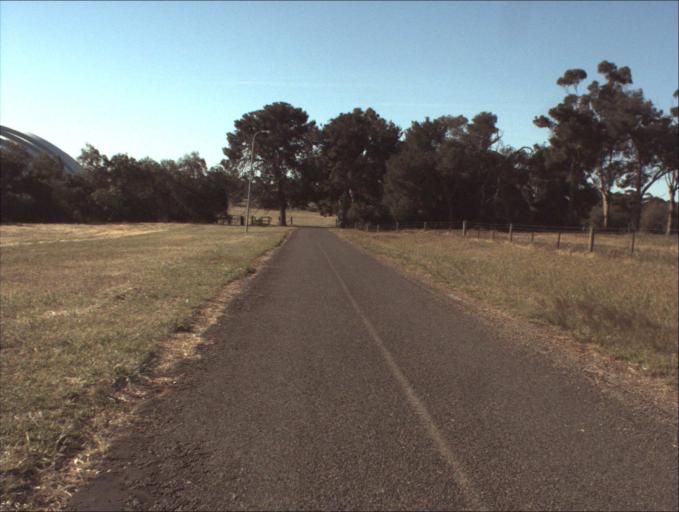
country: AU
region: South Australia
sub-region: Port Adelaide Enfield
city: Enfield
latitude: -34.8442
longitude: 138.6138
